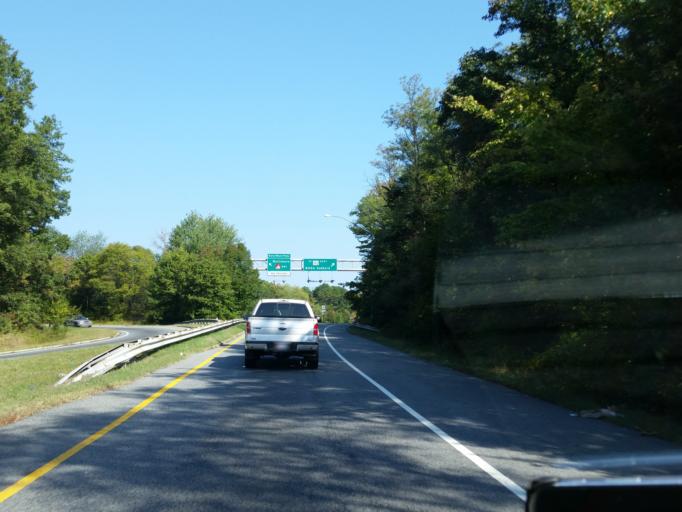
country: US
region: Maryland
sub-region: Prince George's County
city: Greenbelt
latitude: 38.9911
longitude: -76.8838
